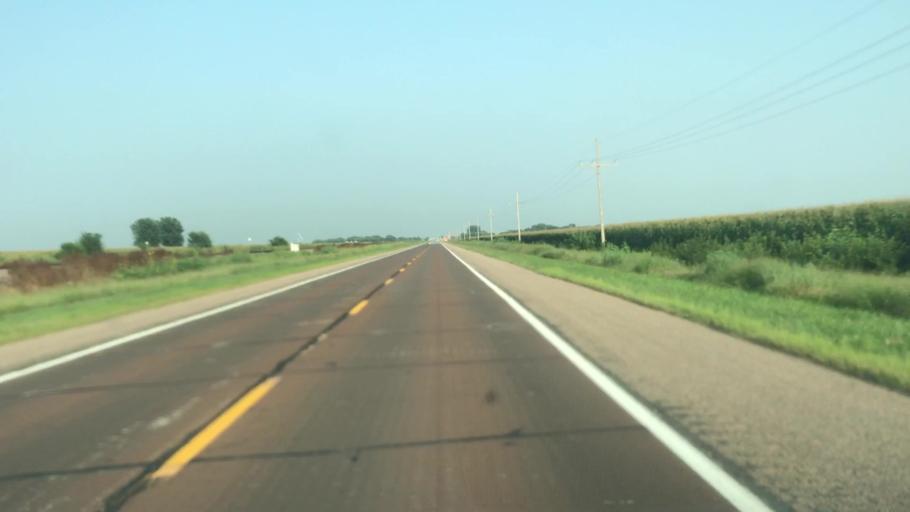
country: US
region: Nebraska
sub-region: Hall County
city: Grand Island
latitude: 40.9642
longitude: -98.4329
